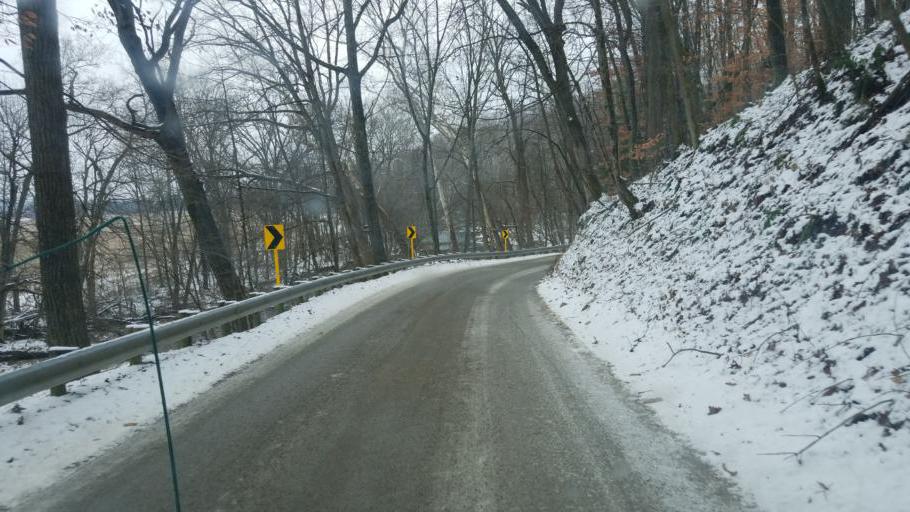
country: US
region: Ohio
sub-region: Sandusky County
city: Bellville
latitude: 40.6071
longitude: -82.4914
